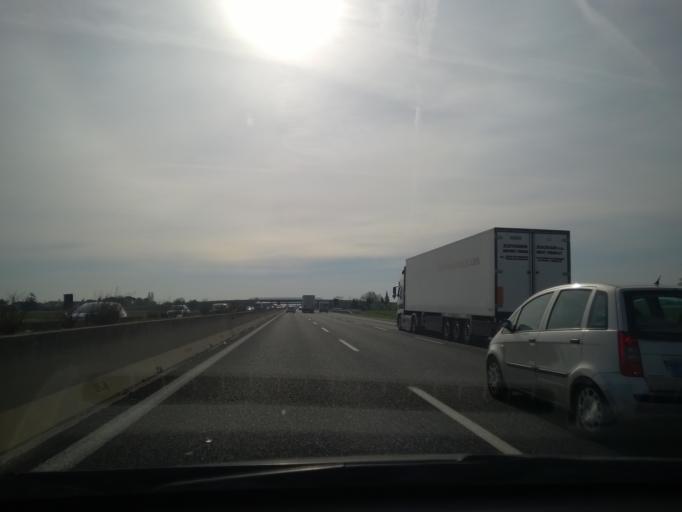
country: IT
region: Emilia-Romagna
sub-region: Forli-Cesena
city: Forlimpopoli
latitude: 44.2452
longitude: 12.1145
